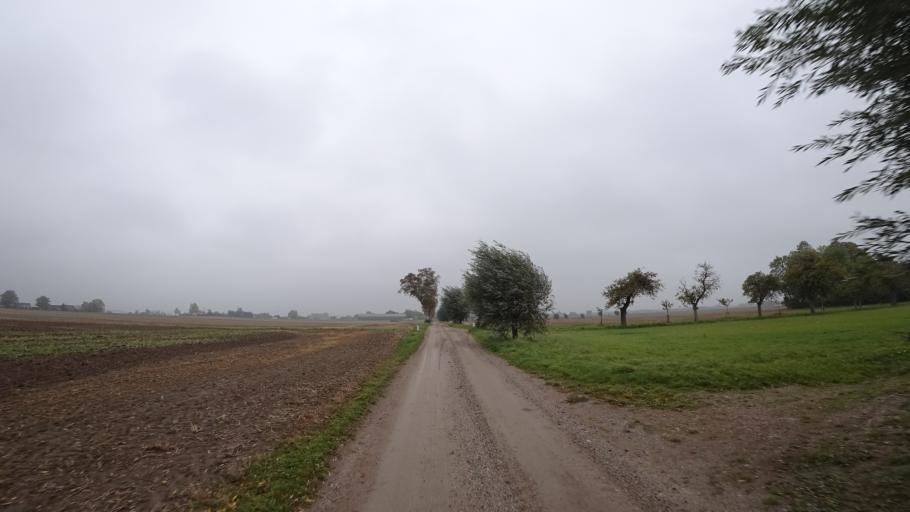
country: SE
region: Skane
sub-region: Kavlinge Kommun
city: Kaevlinge
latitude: 55.8075
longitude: 13.1393
